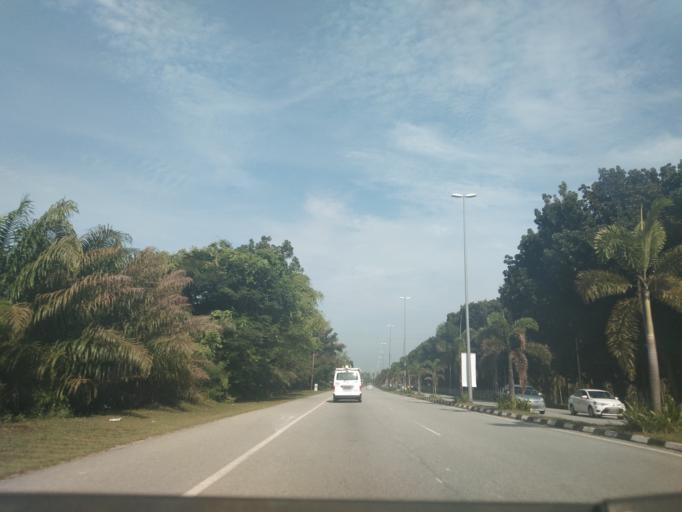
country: MY
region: Perak
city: Ipoh
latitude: 4.5012
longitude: 101.1417
